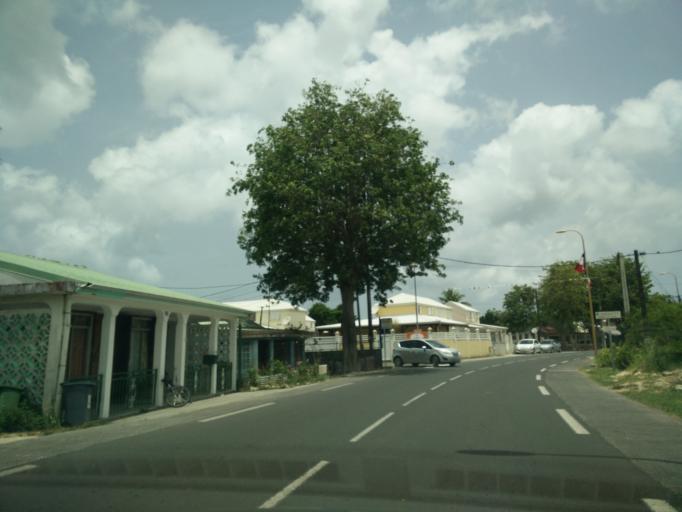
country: GP
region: Guadeloupe
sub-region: Guadeloupe
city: Port-Louis
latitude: 16.4154
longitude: -61.5267
